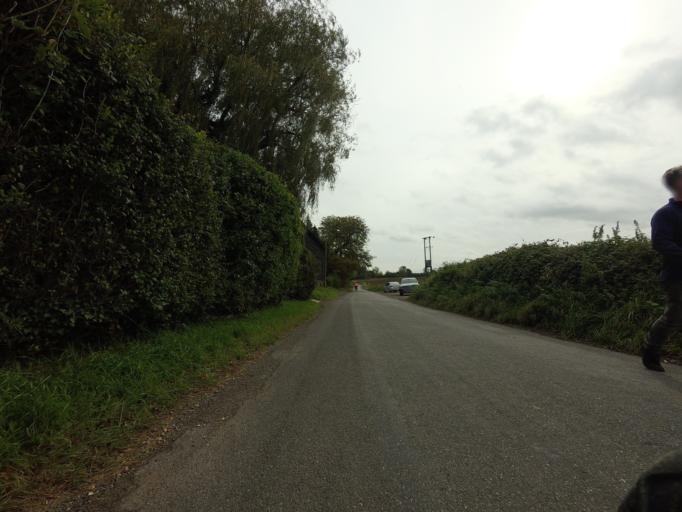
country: GB
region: England
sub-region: Hertfordshire
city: Reed
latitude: 51.9794
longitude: 0.0500
